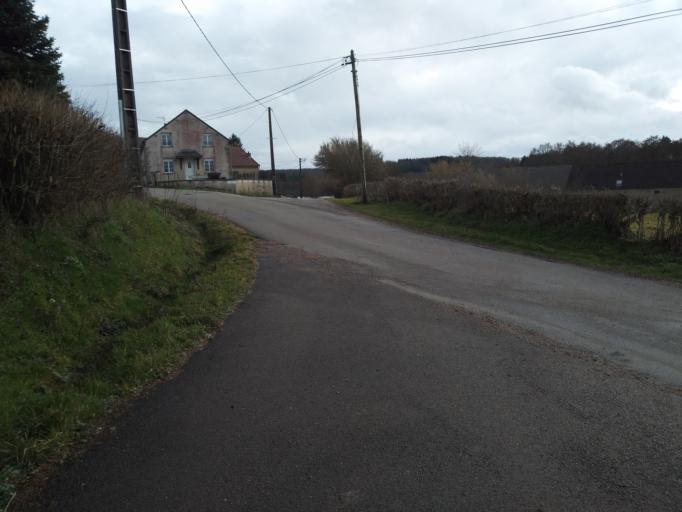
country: FR
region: Bourgogne
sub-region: Departement de la Cote-d'Or
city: Saulieu
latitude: 47.2771
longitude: 4.1433
